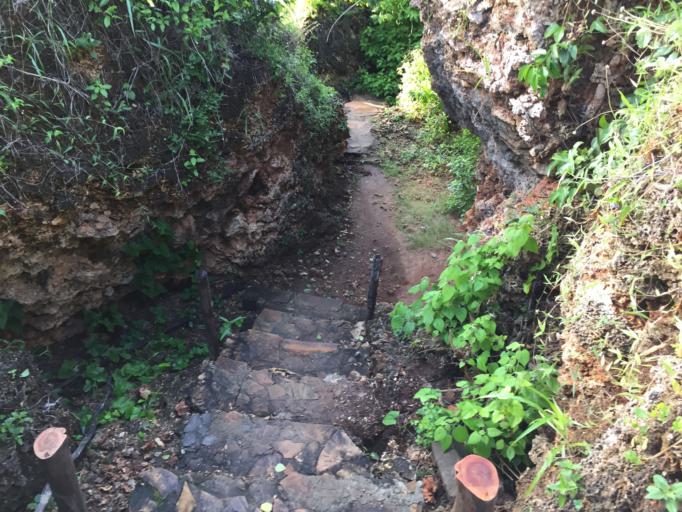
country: TZ
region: Pwani
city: Vikindu
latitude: -7.0160
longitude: 39.5479
